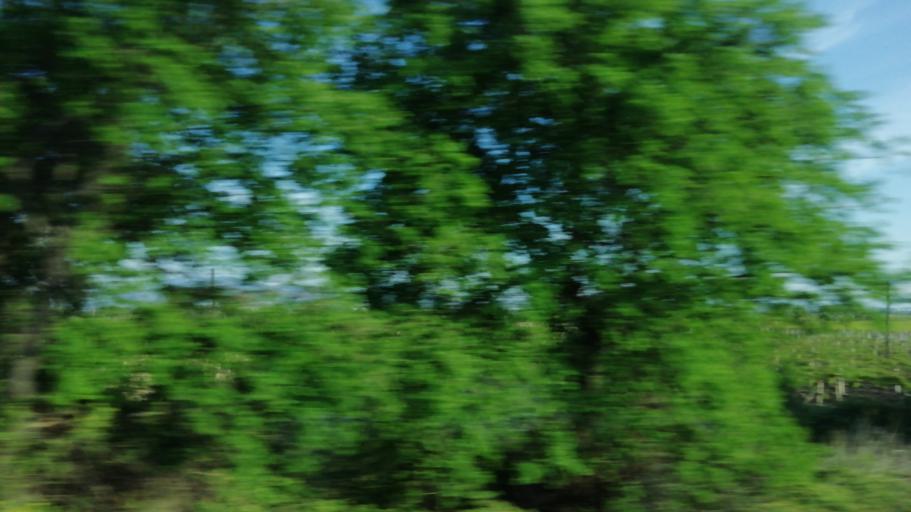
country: TR
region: Manisa
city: Saruhanli
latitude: 38.7375
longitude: 27.5962
